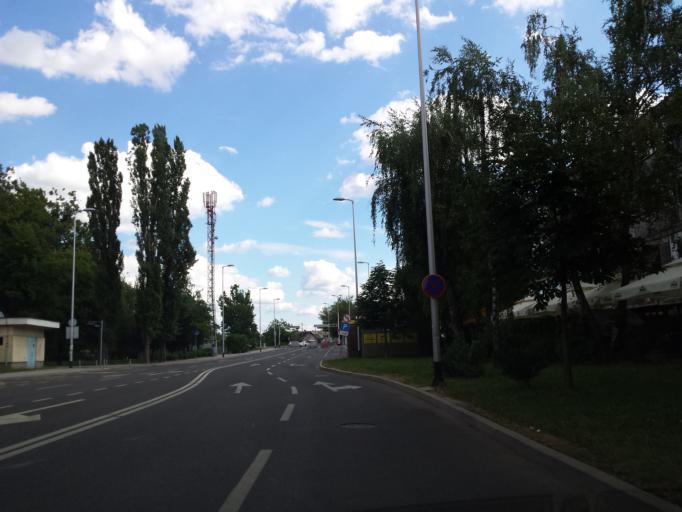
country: HR
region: Grad Zagreb
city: Novi Zagreb
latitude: 45.7685
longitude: 15.9456
